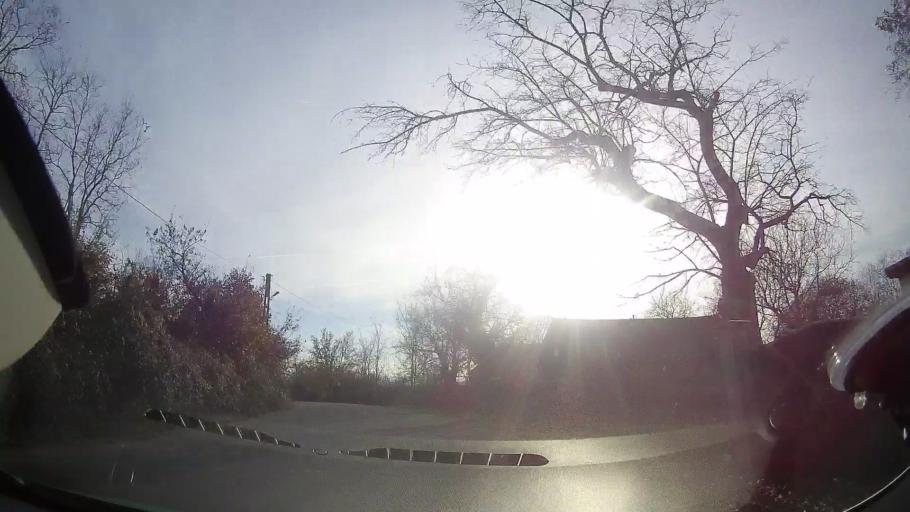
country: RO
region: Bihor
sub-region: Comuna Sarbi
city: Burzuc
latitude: 47.1179
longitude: 22.1791
